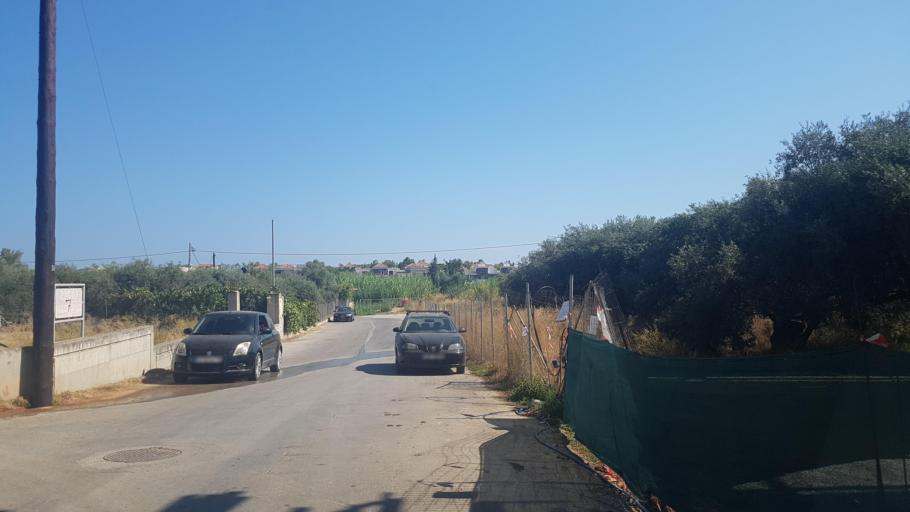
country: GR
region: Crete
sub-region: Nomos Chanias
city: Daratsos
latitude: 35.5092
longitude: 23.9803
